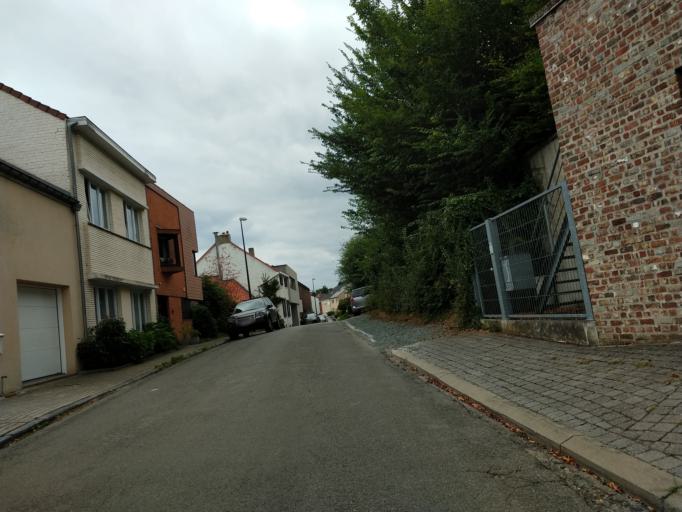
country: BE
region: Flanders
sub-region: Provincie Vlaams-Brabant
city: Tervuren
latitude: 50.8340
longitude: 4.5521
